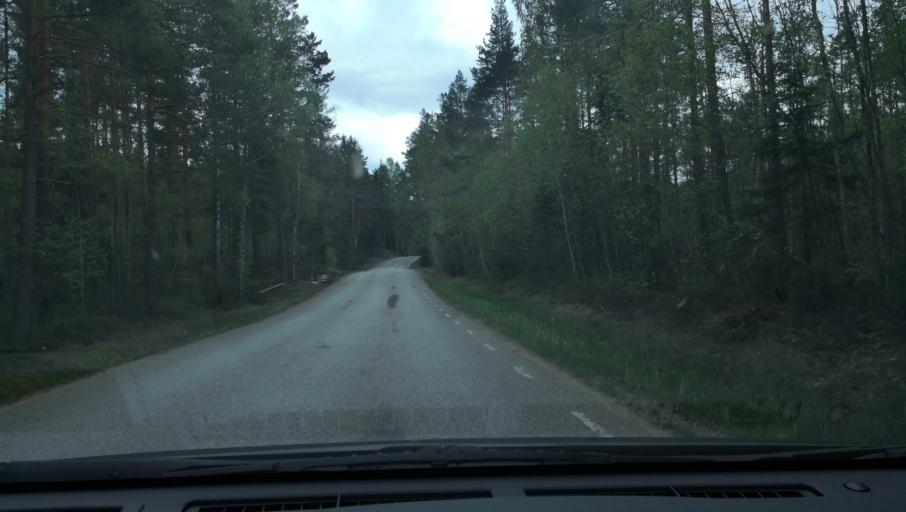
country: SE
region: Vaestmanland
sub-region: Skinnskattebergs Kommun
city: Skinnskatteberg
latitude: 59.8183
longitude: 15.5533
